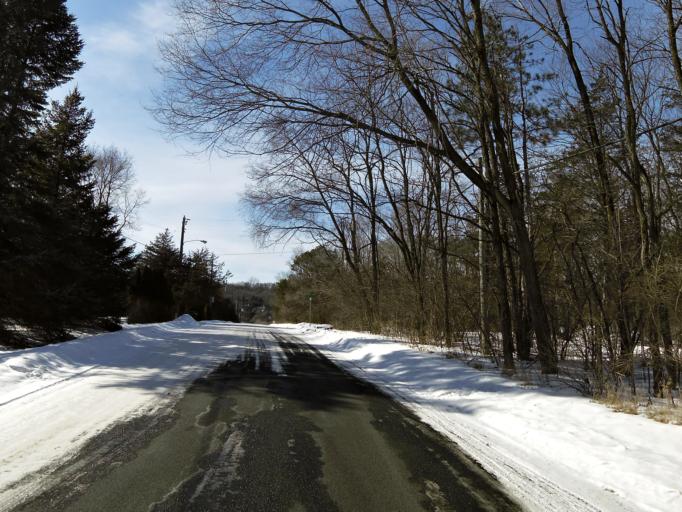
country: US
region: Minnesota
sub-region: Washington County
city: Lake Saint Croix Beach
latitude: 44.9321
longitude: -92.7686
